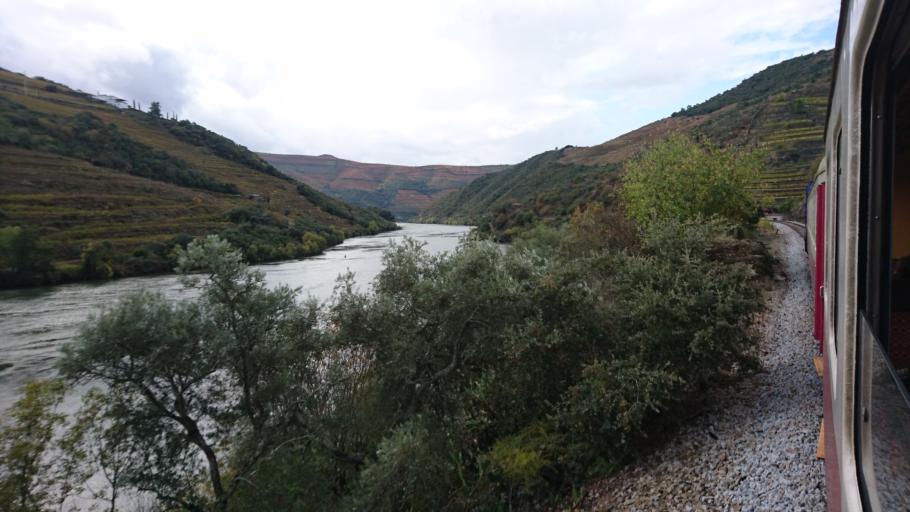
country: PT
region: Vila Real
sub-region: Sabrosa
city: Sabrosa
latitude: 41.1986
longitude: -7.5075
